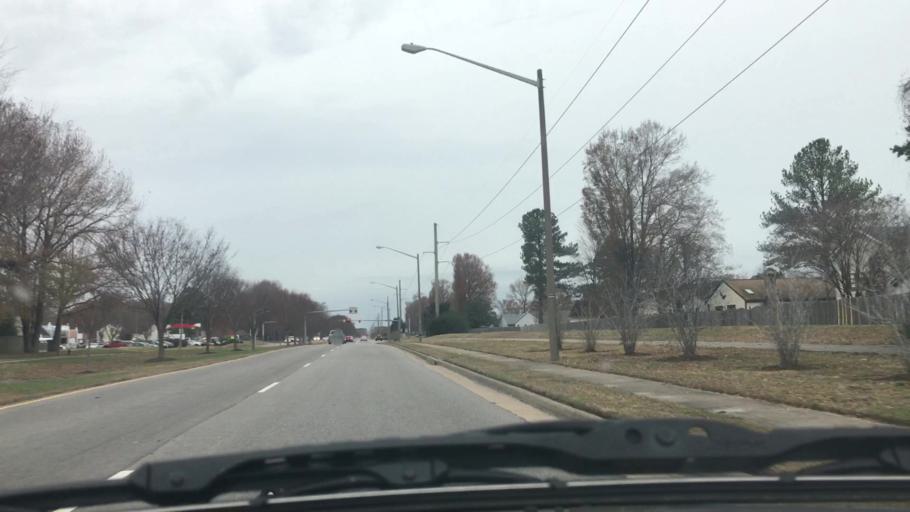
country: US
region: Virginia
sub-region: City of Virginia Beach
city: Virginia Beach
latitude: 36.8003
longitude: -76.1100
